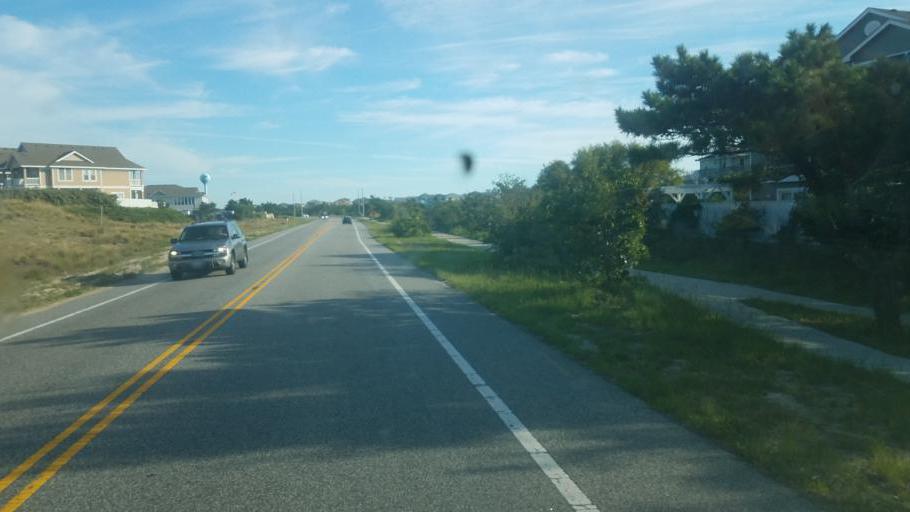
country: US
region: North Carolina
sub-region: Dare County
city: Southern Shores
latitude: 36.2994
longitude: -75.8041
